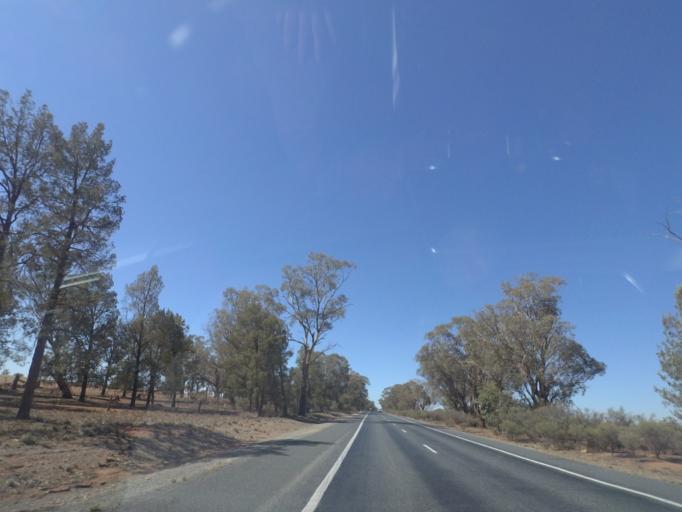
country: AU
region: New South Wales
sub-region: Bland
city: West Wyalong
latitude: -34.2083
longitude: 147.1092
